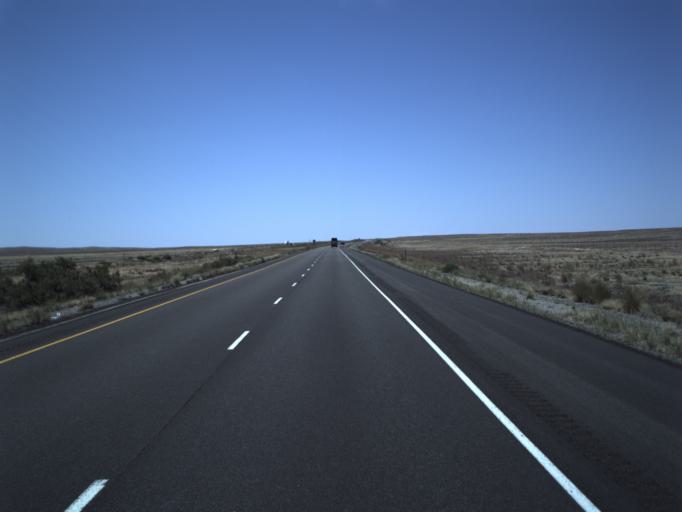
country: US
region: Colorado
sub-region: Mesa County
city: Loma
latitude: 39.0734
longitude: -109.2364
